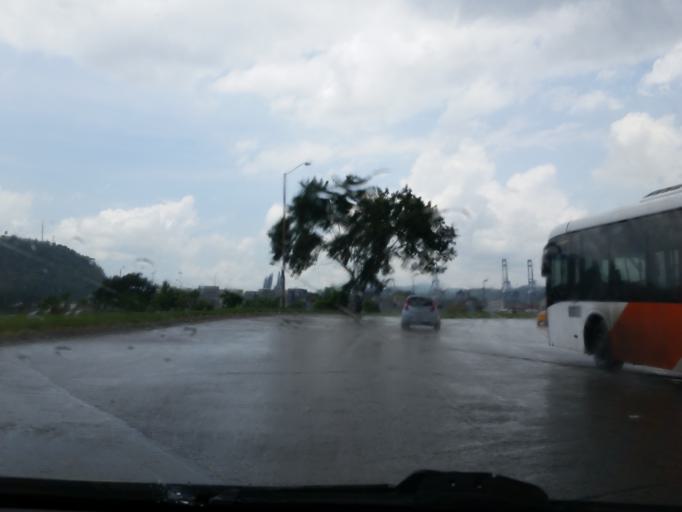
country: PA
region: Panama
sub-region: Distrito de Panama
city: Ancon
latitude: 8.9640
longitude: -79.5548
